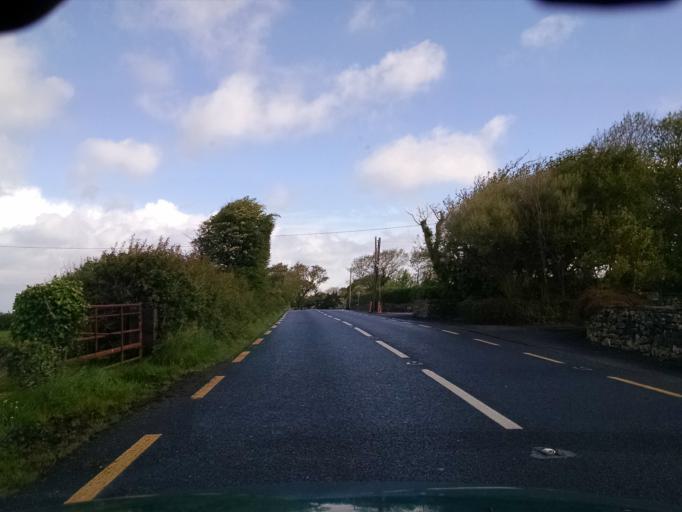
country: IE
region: Connaught
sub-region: County Galway
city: Bearna
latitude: 53.1262
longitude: -9.1233
